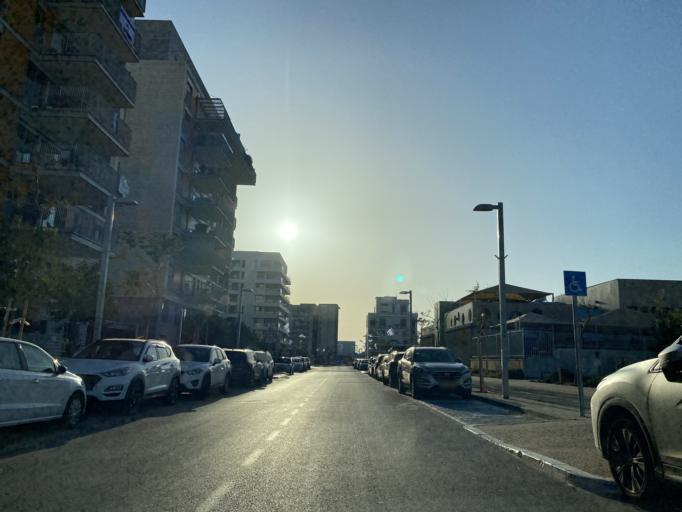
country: IL
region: Tel Aviv
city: Herzliyya
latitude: 32.1618
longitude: 34.8305
